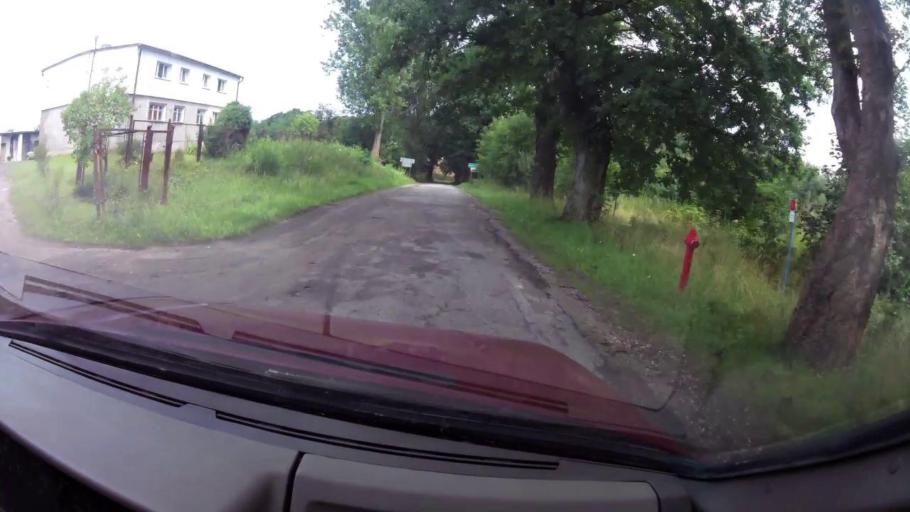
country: PL
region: West Pomeranian Voivodeship
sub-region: Powiat swidwinski
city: Polczyn-Zdroj
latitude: 53.7973
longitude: 16.0462
